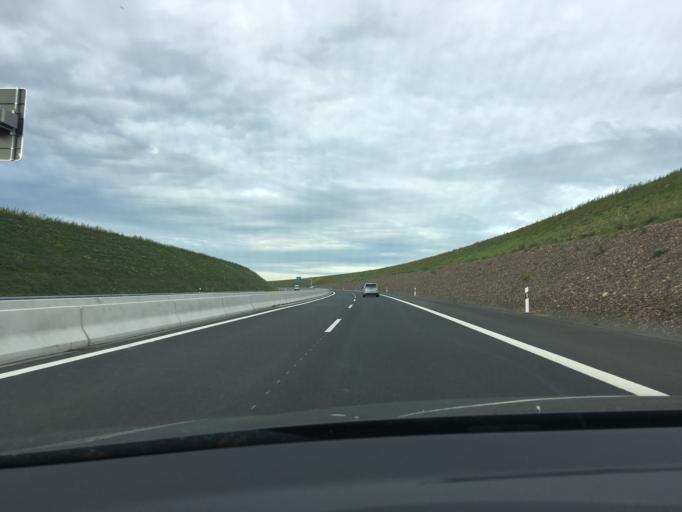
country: DE
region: Saxony
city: Borna
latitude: 51.1563
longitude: 12.5018
